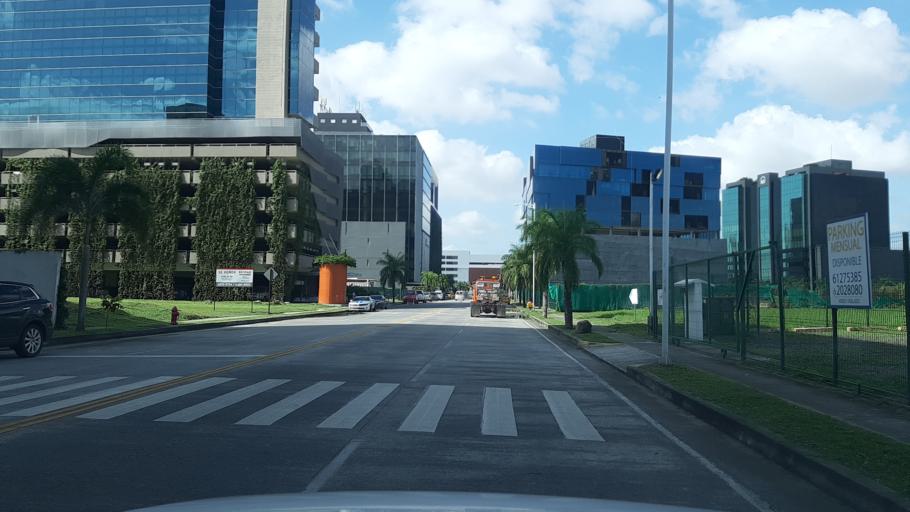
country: PA
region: Panama
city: San Miguelito
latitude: 9.0289
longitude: -79.4603
